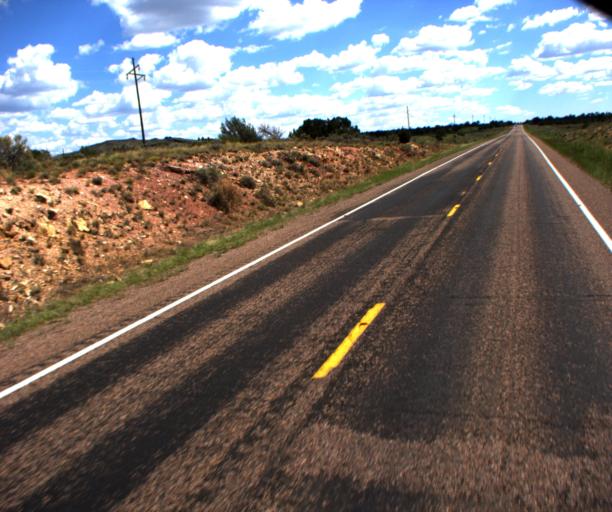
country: US
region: Arizona
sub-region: Coconino County
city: Williams
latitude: 35.5634
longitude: -112.1570
